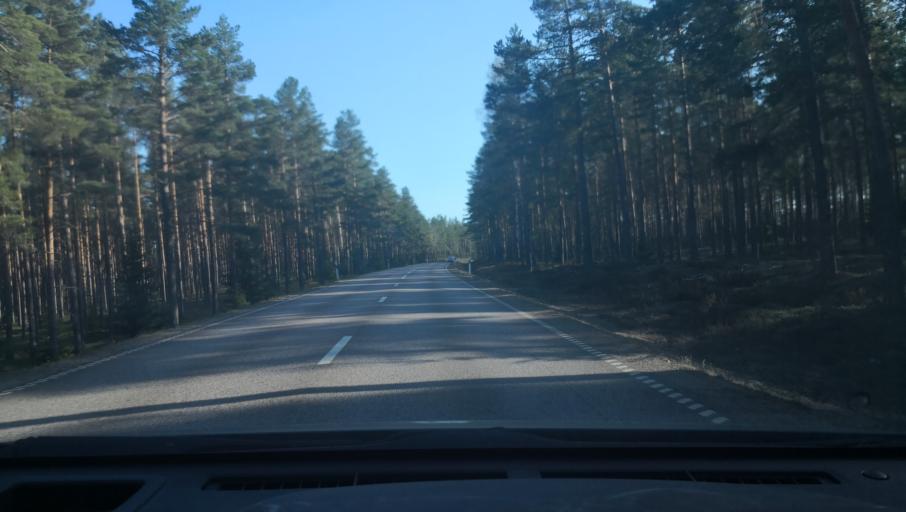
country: SE
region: Uppsala
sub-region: Heby Kommun
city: Tarnsjo
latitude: 60.1082
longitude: 16.8854
